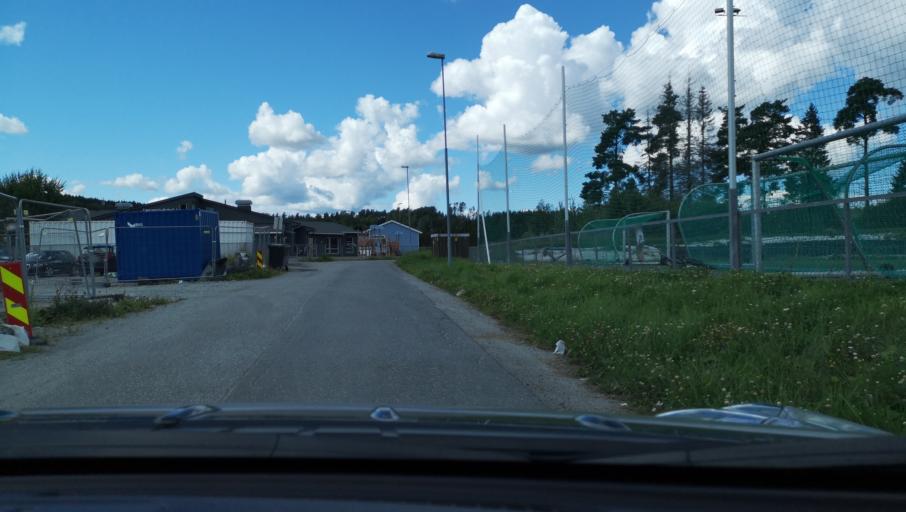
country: NO
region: Ostfold
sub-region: Hobol
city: Tomter
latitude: 59.6646
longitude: 10.9992
